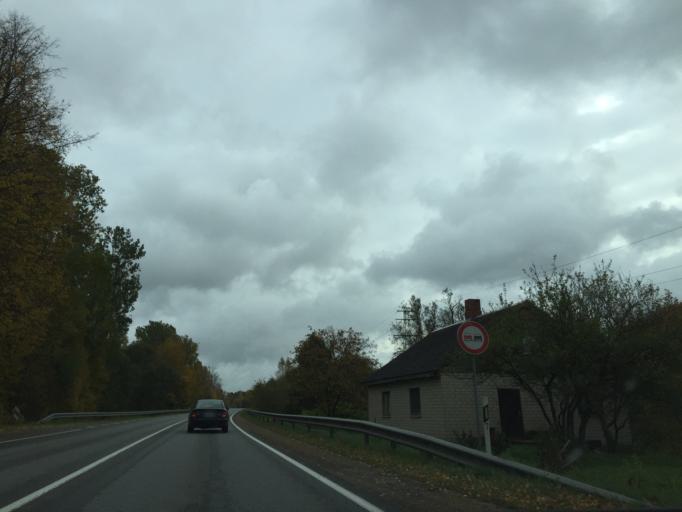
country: LV
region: Kegums
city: Kegums
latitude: 56.7594
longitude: 24.6953
